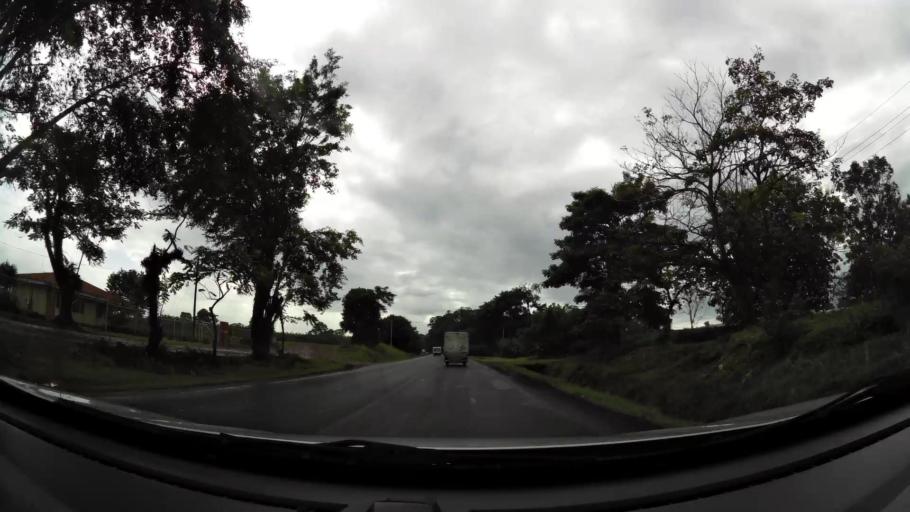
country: CR
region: Limon
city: Pocora
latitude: 10.1561
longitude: -83.5949
